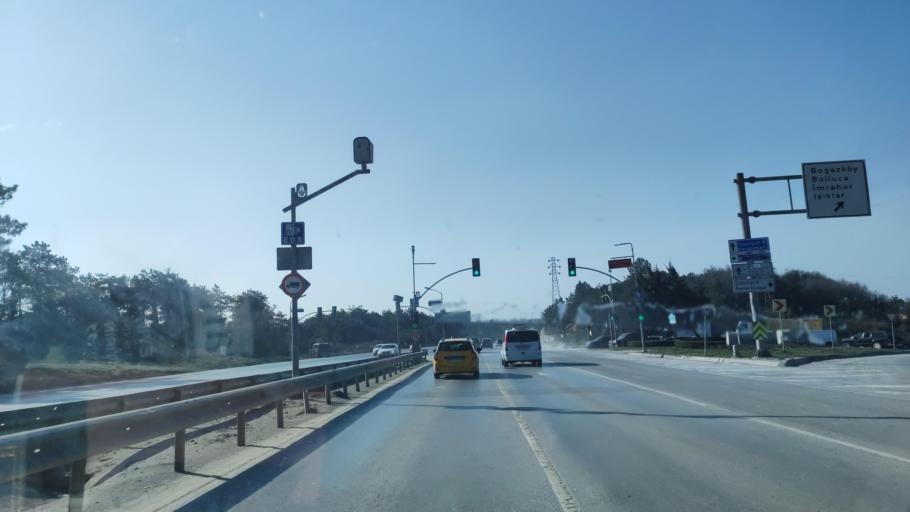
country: TR
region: Istanbul
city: Basaksehir
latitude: 41.1613
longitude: 28.7751
